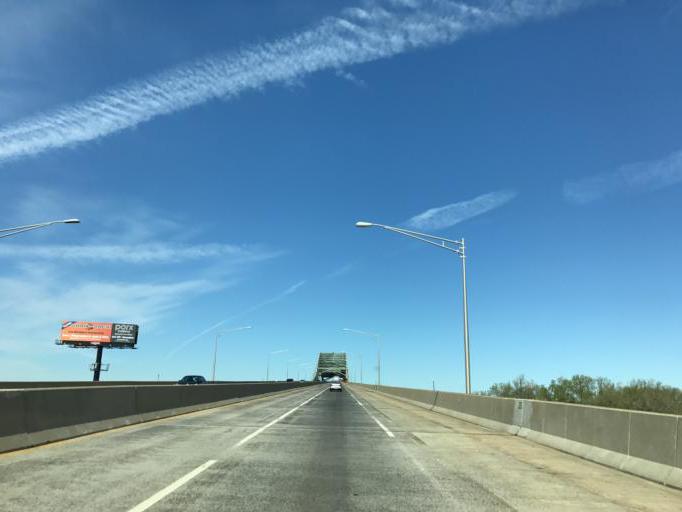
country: US
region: Pennsylvania
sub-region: Bucks County
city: Tullytown
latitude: 40.1152
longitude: -74.8238
